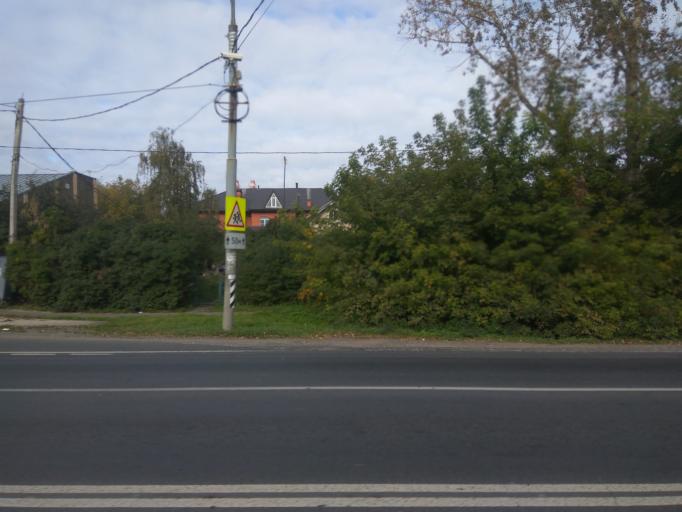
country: RU
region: Moskovskaya
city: Medvezh'i Ozera
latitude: 55.8623
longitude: 37.9875
